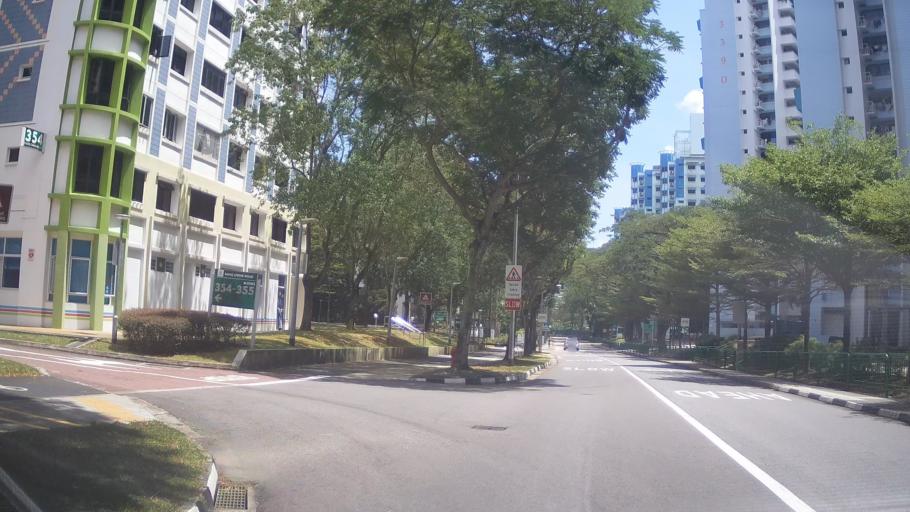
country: MY
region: Johor
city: Johor Bahru
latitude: 1.3385
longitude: 103.7211
